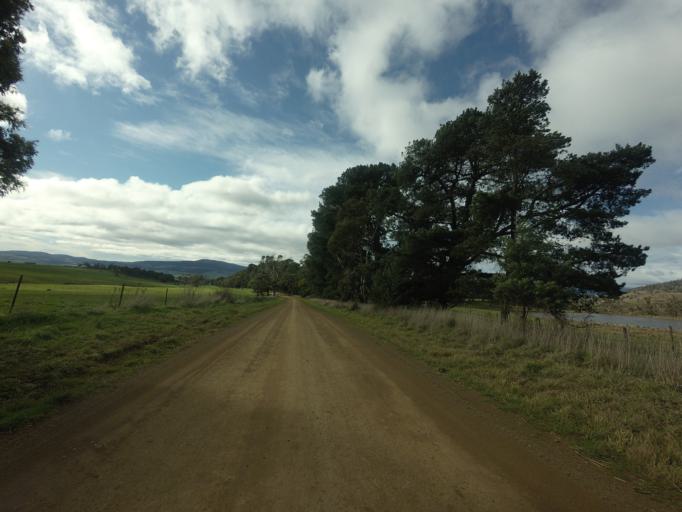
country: AU
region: Tasmania
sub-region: Derwent Valley
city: New Norfolk
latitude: -42.7176
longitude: 146.8769
